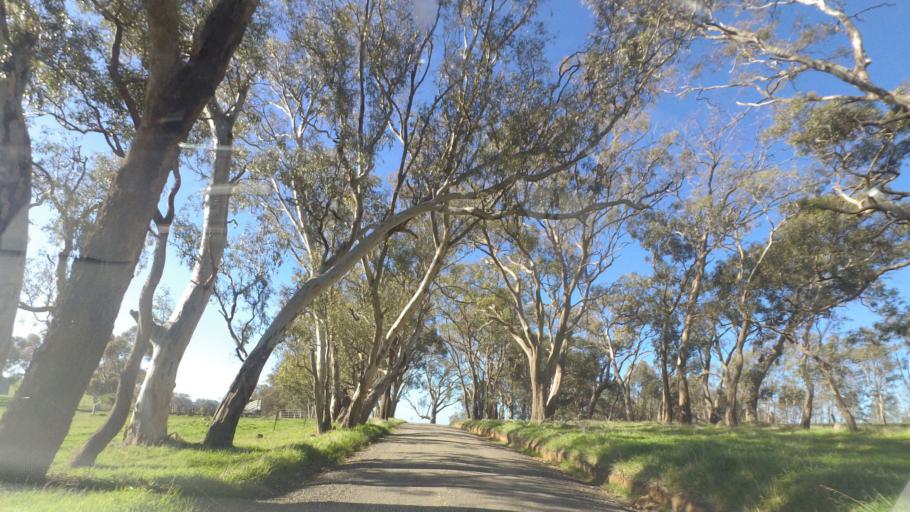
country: AU
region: Victoria
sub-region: Mount Alexander
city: Castlemaine
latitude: -36.9617
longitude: 144.3349
